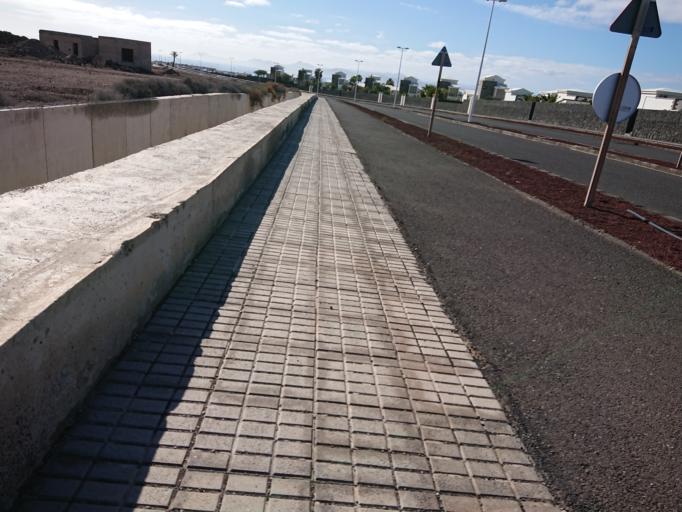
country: ES
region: Canary Islands
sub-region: Provincia de Las Palmas
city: Playa Blanca
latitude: 28.8716
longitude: -13.8637
